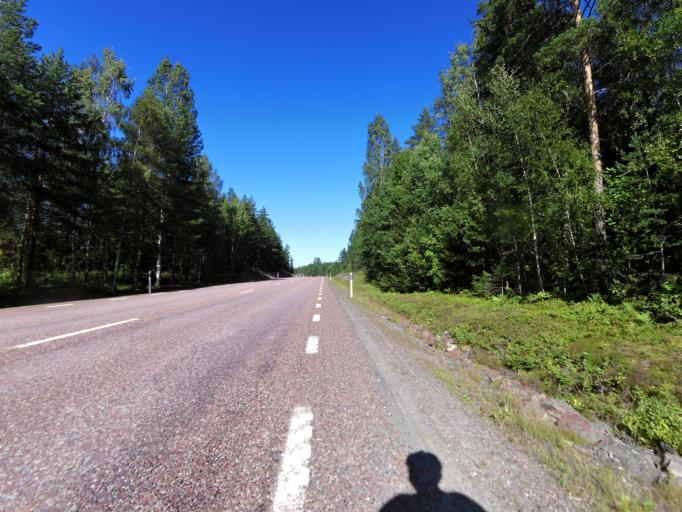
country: SE
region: Gaevleborg
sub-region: Hofors Kommun
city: Hofors
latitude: 60.5464
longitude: 16.4708
